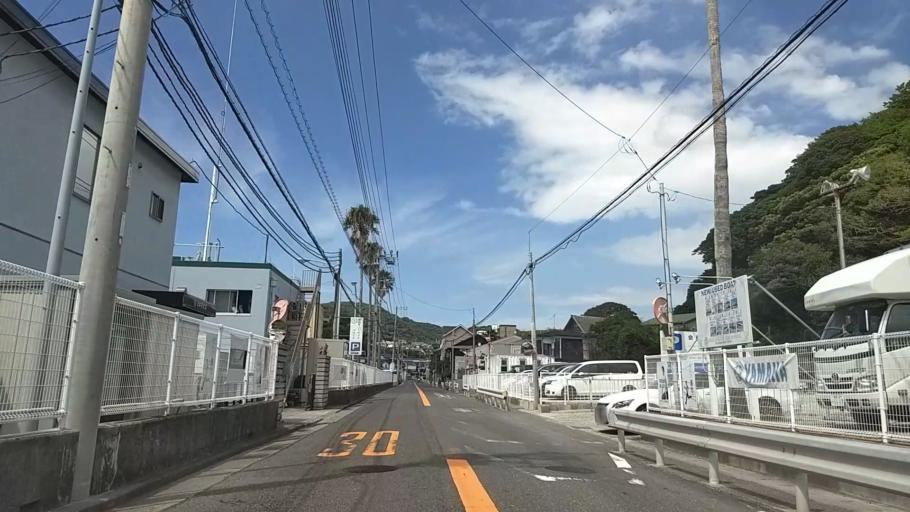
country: JP
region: Kanagawa
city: Hayama
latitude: 35.2297
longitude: 139.6036
